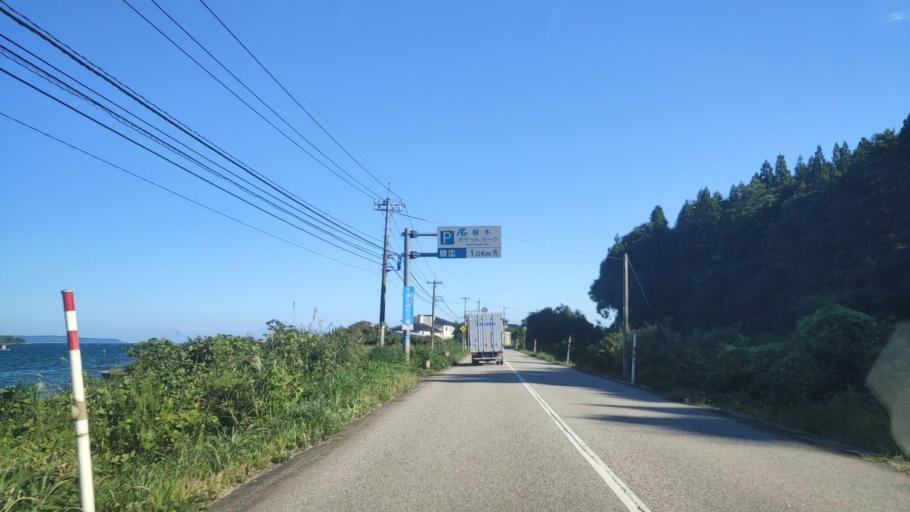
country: JP
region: Ishikawa
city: Nanao
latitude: 37.2001
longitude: 136.9076
